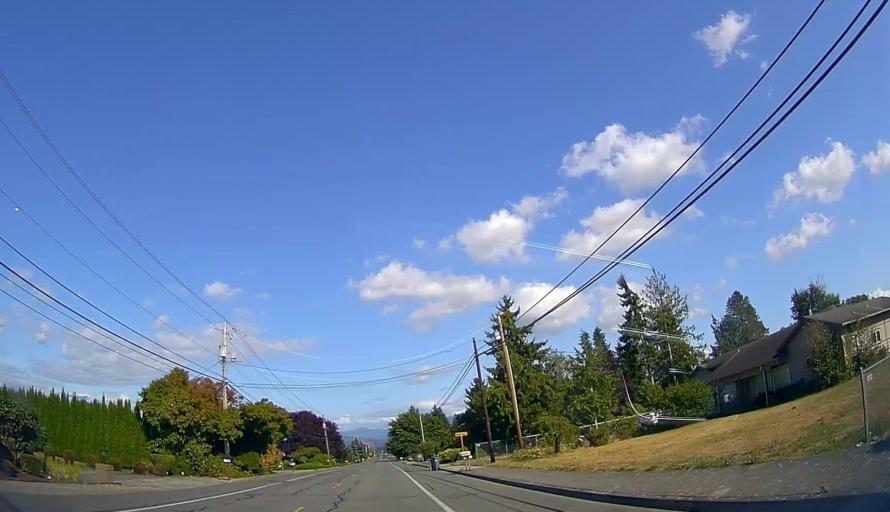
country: US
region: Washington
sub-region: Skagit County
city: Burlington
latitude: 48.4722
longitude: -122.3888
